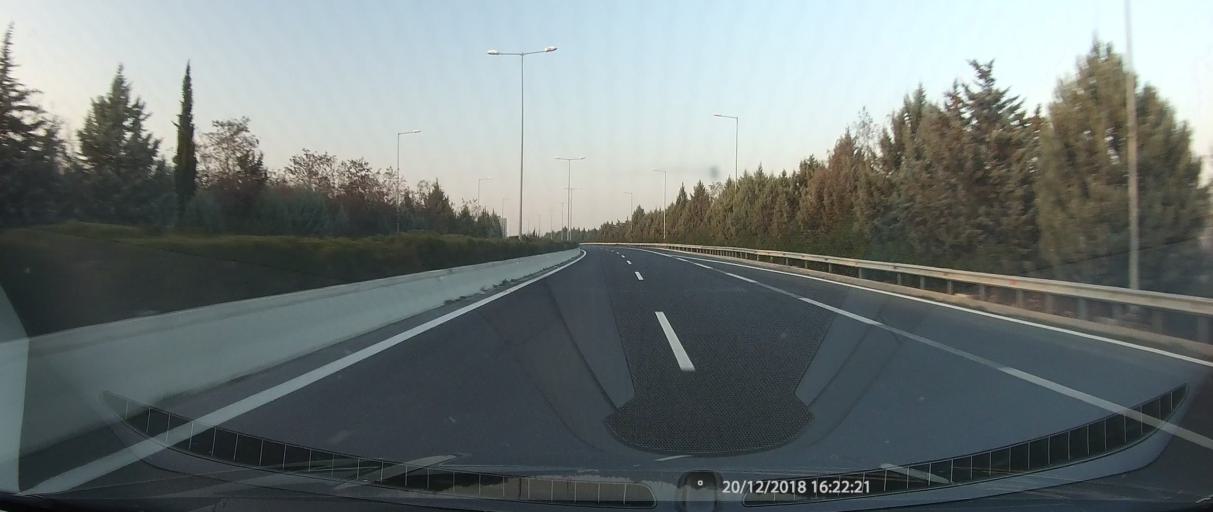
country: GR
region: Thessaly
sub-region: Nomos Magnisias
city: Sourpi
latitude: 39.0681
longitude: 22.8872
